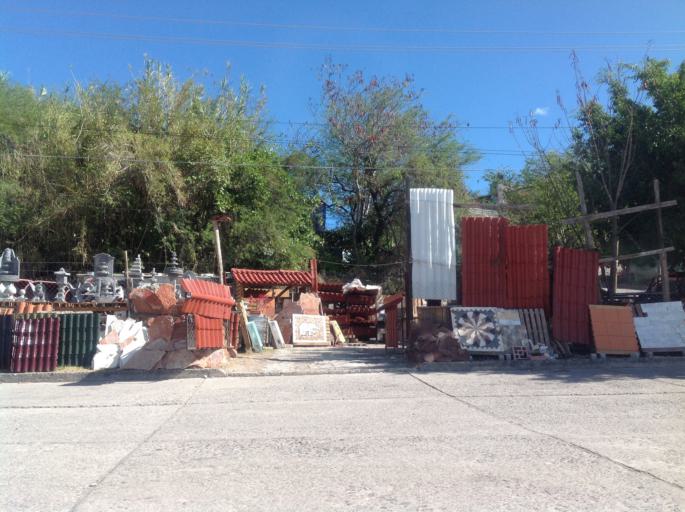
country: MX
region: Oaxaca
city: Ciudad de Huajuapam de Leon
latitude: 17.8138
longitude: -97.7633
